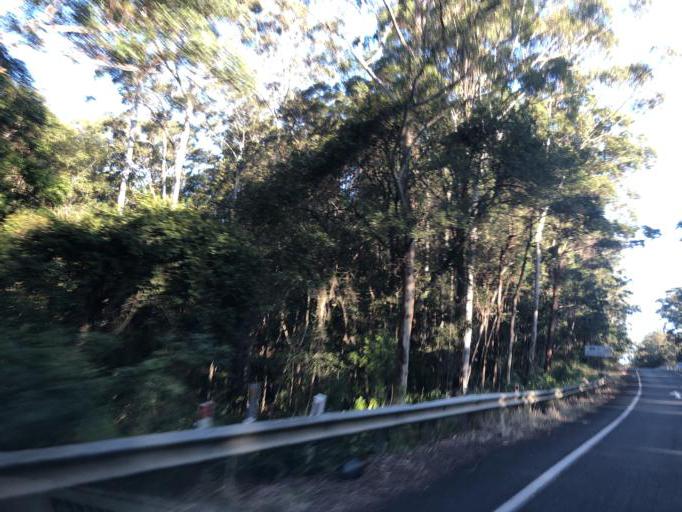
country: AU
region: New South Wales
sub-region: Nambucca Shire
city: Nambucca
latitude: -30.5524
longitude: 153.0078
